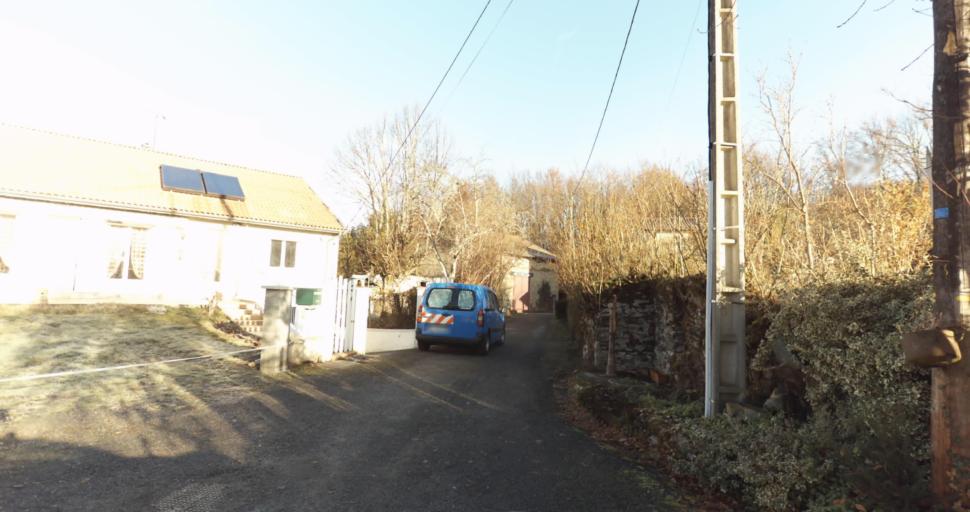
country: FR
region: Limousin
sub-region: Departement de la Haute-Vienne
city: Aixe-sur-Vienne
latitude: 45.8019
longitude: 1.1295
